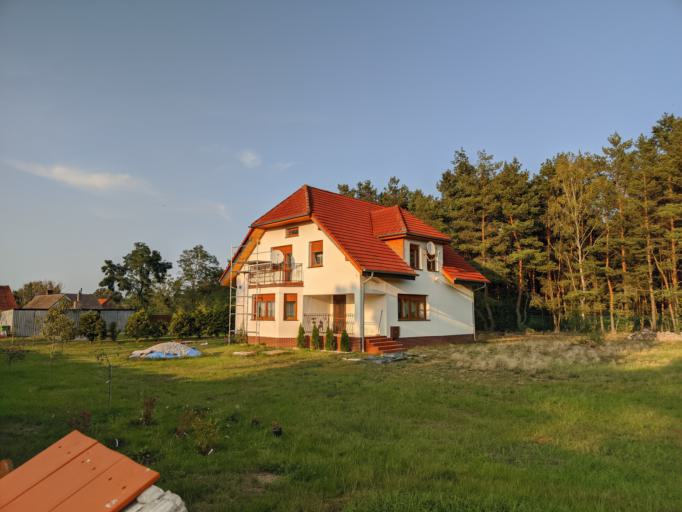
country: PL
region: Lubusz
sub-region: Powiat krosnienski
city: Maszewo
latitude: 52.0625
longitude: 14.8007
